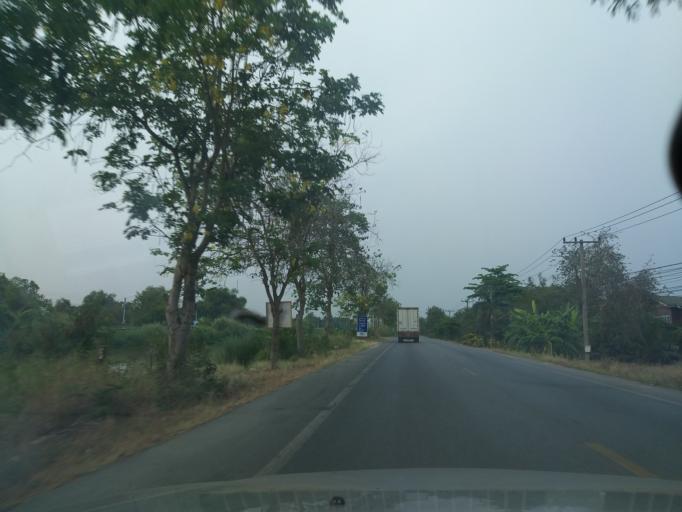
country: TH
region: Pathum Thani
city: Ban Lam Luk Ka
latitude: 14.0029
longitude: 100.8948
